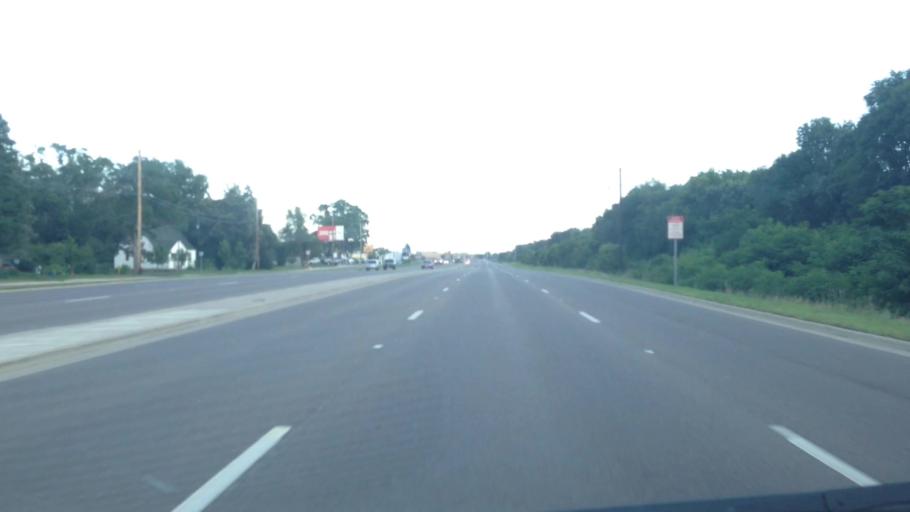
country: US
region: Minnesota
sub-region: Hennepin County
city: Brooklyn Park
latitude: 45.0656
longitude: -93.3657
